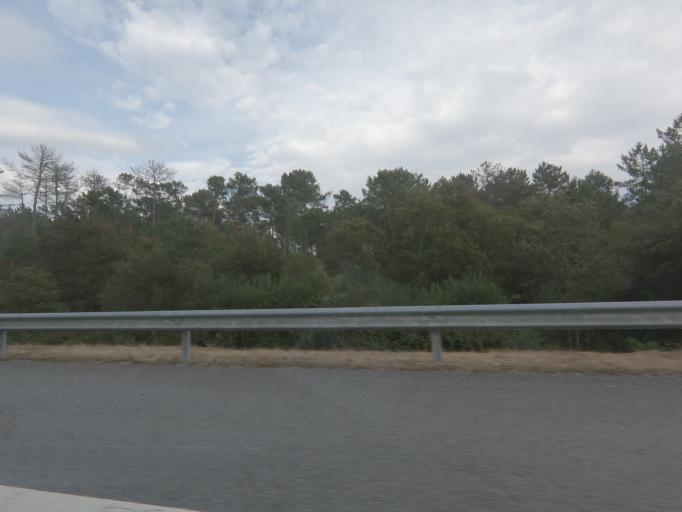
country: PT
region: Viseu
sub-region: Viseu
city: Campo
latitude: 40.7230
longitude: -7.9228
